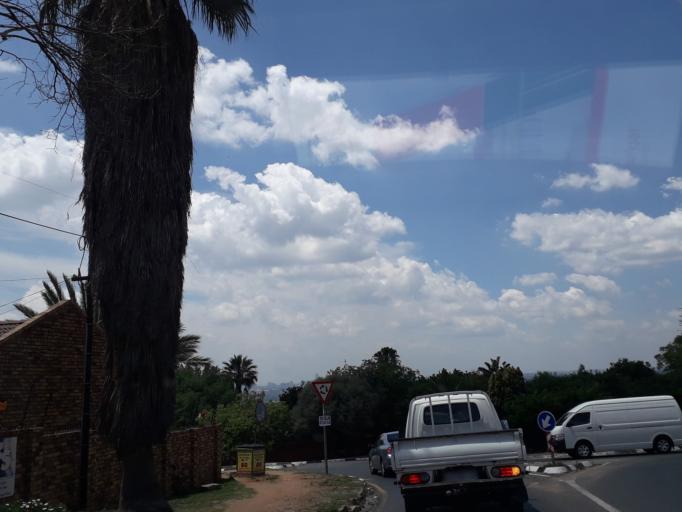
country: ZA
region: Gauteng
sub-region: West Rand District Municipality
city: Muldersdriseloop
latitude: -26.0772
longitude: 27.9283
